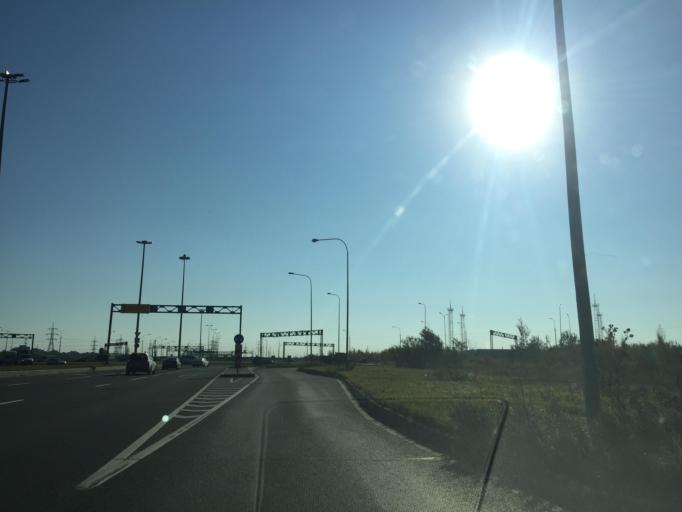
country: RU
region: St.-Petersburg
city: Metallostroy
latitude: 59.7496
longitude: 30.5292
